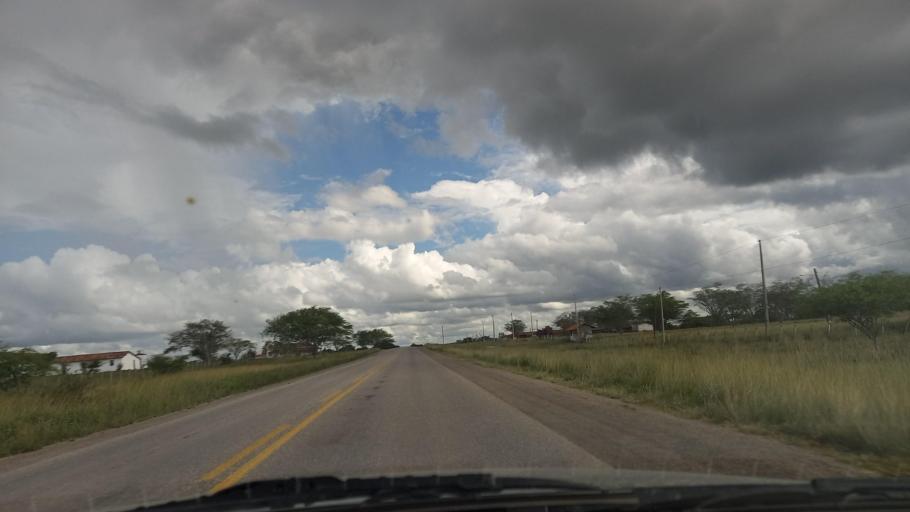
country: BR
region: Pernambuco
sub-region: Cachoeirinha
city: Cachoeirinha
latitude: -8.5270
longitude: -36.2613
